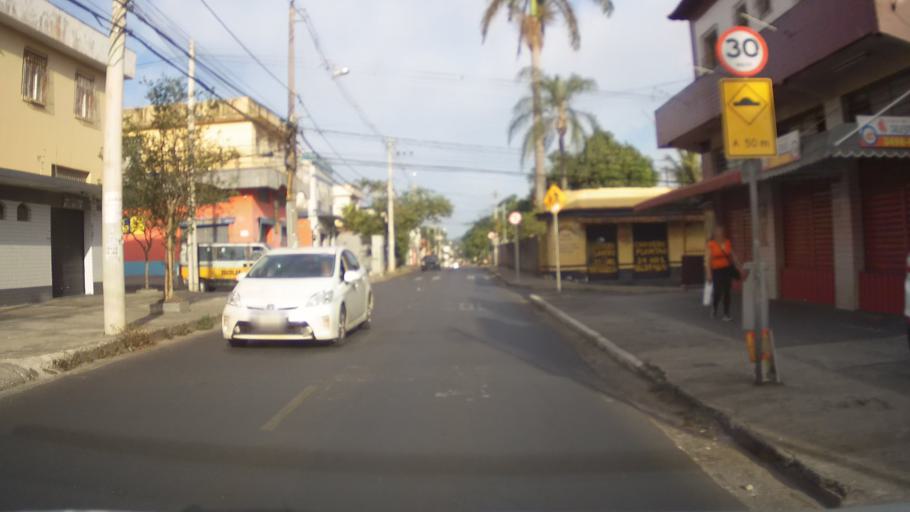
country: BR
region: Minas Gerais
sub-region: Belo Horizonte
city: Belo Horizonte
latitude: -19.8701
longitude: -43.9934
